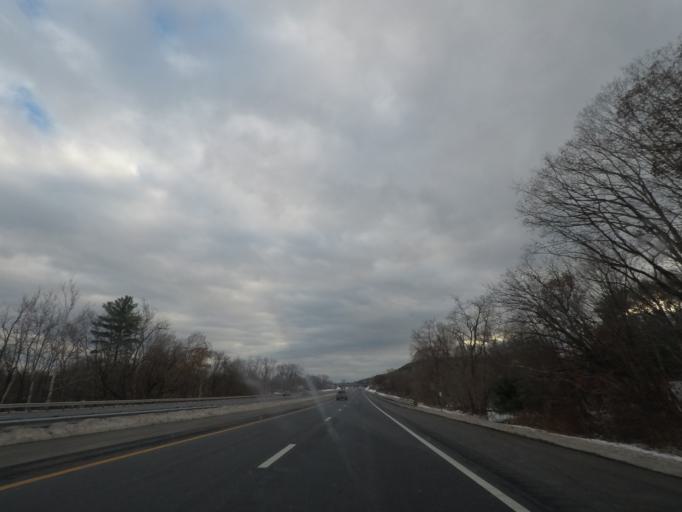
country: US
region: New York
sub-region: Ulster County
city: Lake Katrine
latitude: 41.9822
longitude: -74.0091
